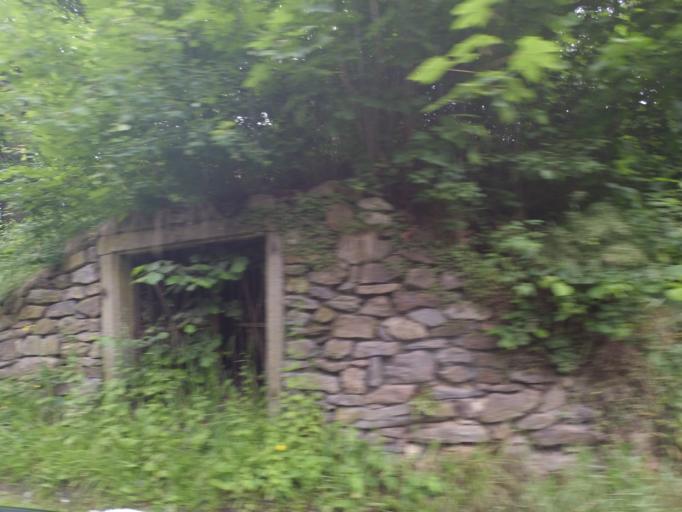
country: DE
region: Bavaria
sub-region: Lower Bavaria
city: Regen
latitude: 48.9719
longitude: 13.1235
